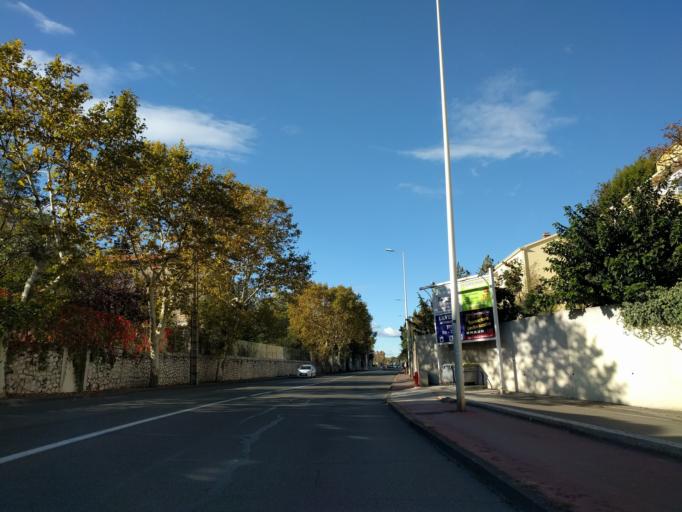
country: FR
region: Languedoc-Roussillon
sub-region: Departement de l'Herault
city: Montpellier
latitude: 43.6265
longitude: 3.8598
